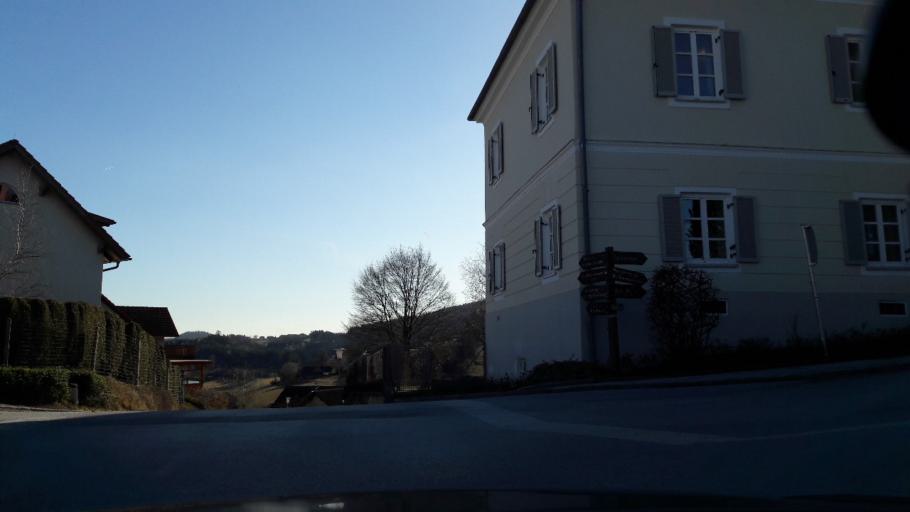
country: AT
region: Styria
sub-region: Politischer Bezirk Graz-Umgebung
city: Eisbach
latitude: 47.1323
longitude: 15.2874
